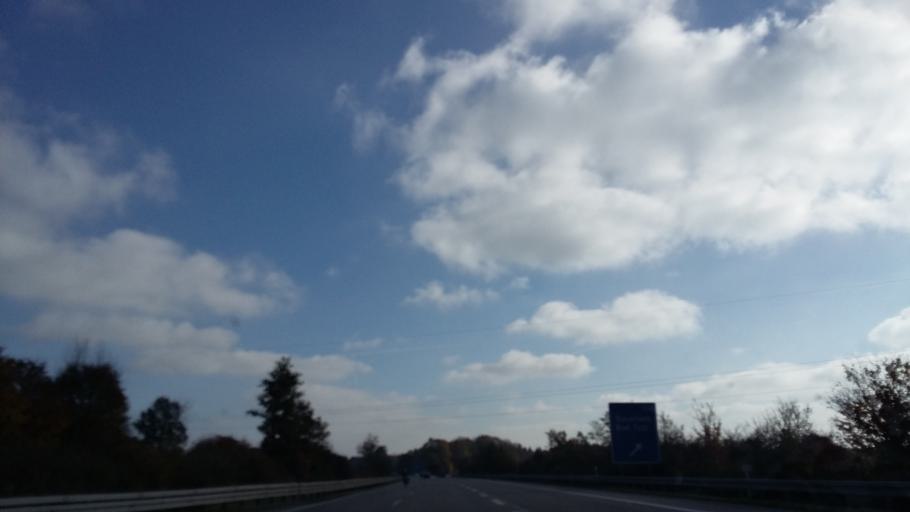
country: DE
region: Bavaria
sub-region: Upper Bavaria
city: Taufkirchen
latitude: 48.0286
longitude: 11.6254
